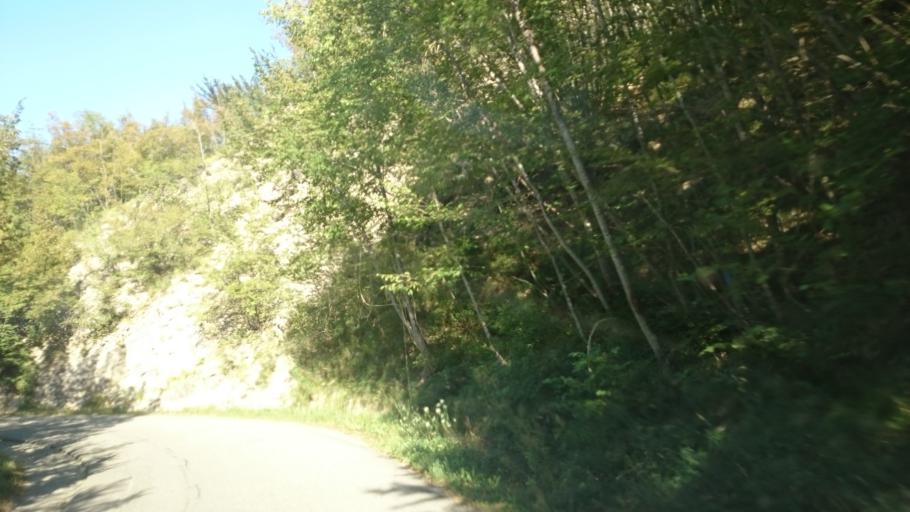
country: IT
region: Emilia-Romagna
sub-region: Provincia di Reggio Emilia
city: Villa Minozzo
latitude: 44.3155
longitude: 10.4683
